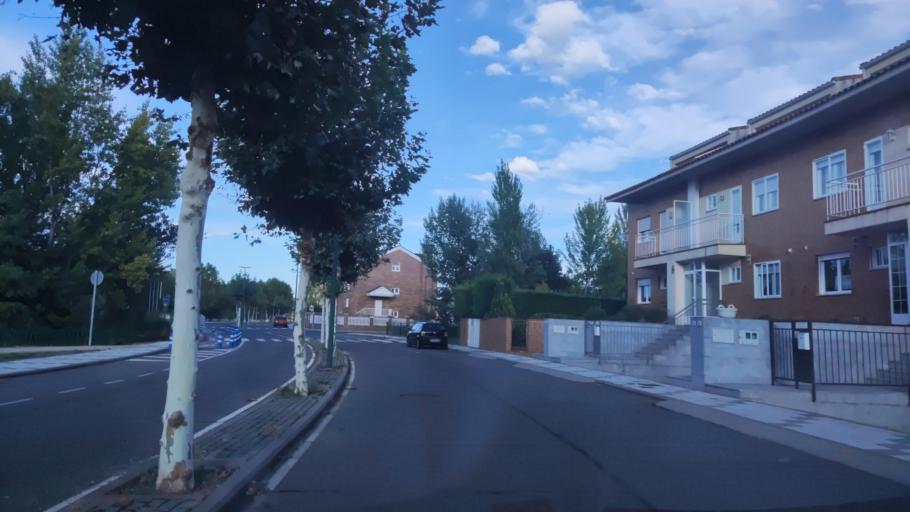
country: ES
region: Castille and Leon
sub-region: Provincia de Salamanca
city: Salamanca
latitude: 40.9548
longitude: -5.6513
